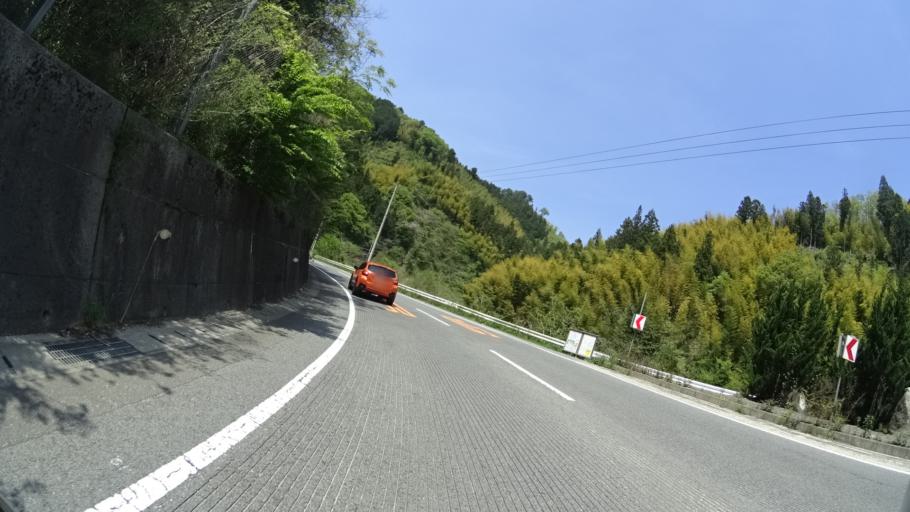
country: JP
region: Ehime
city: Hojo
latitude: 33.9148
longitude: 132.8833
